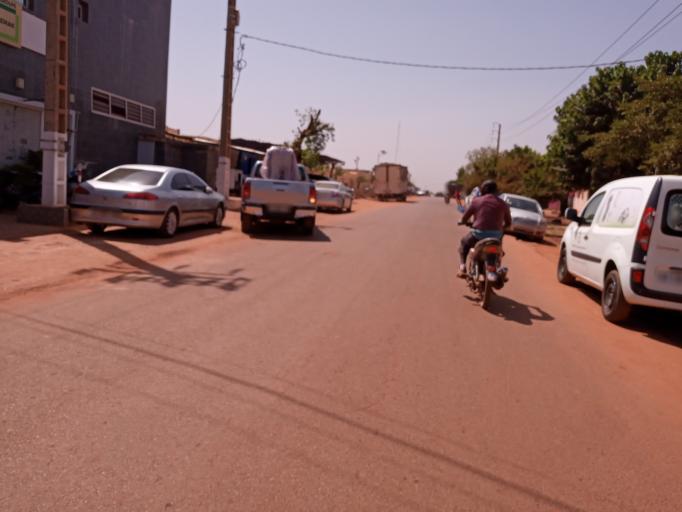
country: ML
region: Bamako
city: Bamako
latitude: 12.6132
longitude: -7.9940
